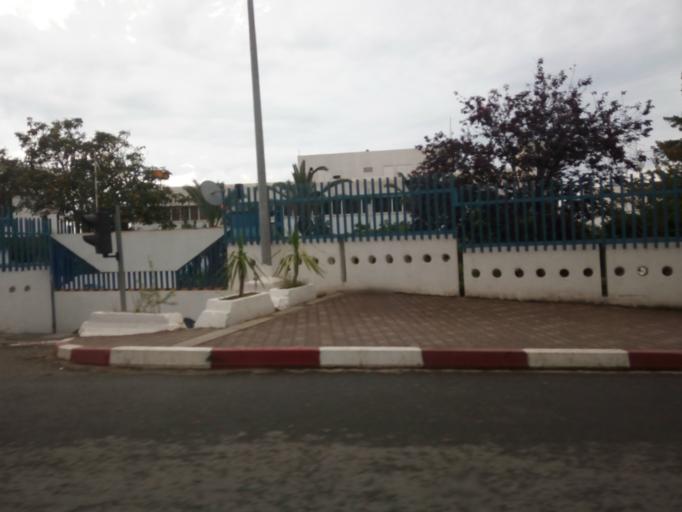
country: DZ
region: Alger
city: Algiers
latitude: 36.7534
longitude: 3.0265
